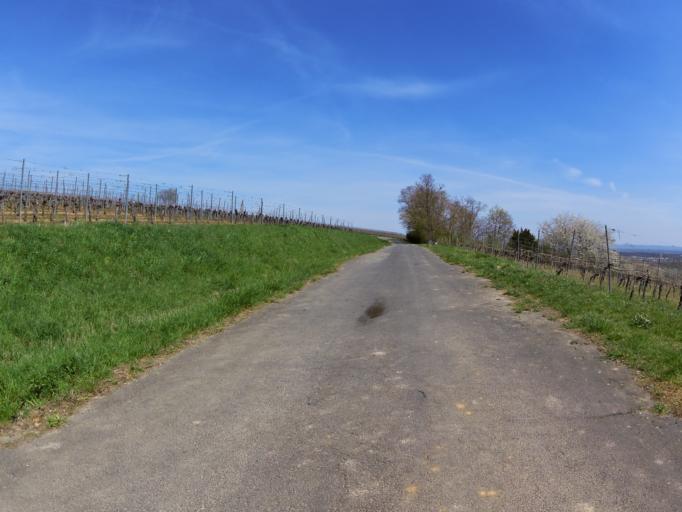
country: DE
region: Bavaria
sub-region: Regierungsbezirk Unterfranken
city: Mainstockheim
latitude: 49.7949
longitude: 10.1463
